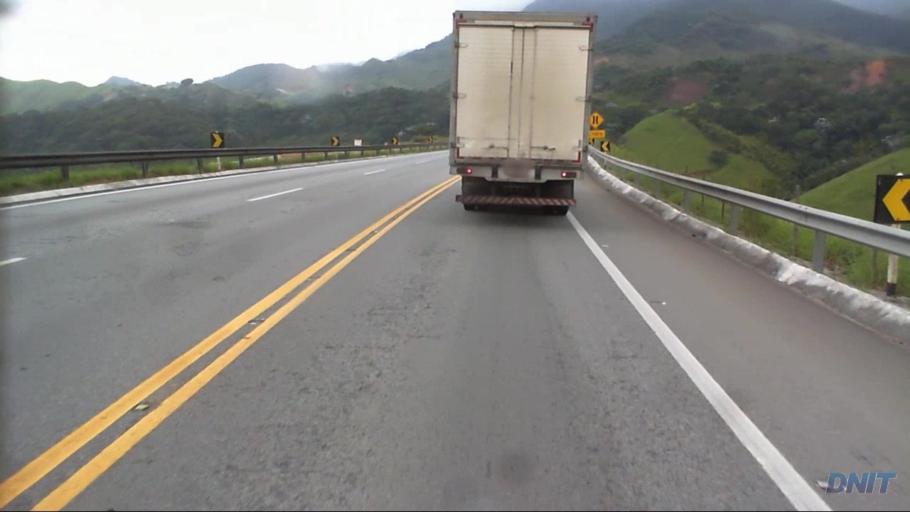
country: BR
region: Minas Gerais
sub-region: Nova Era
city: Nova Era
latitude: -19.6533
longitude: -42.9519
